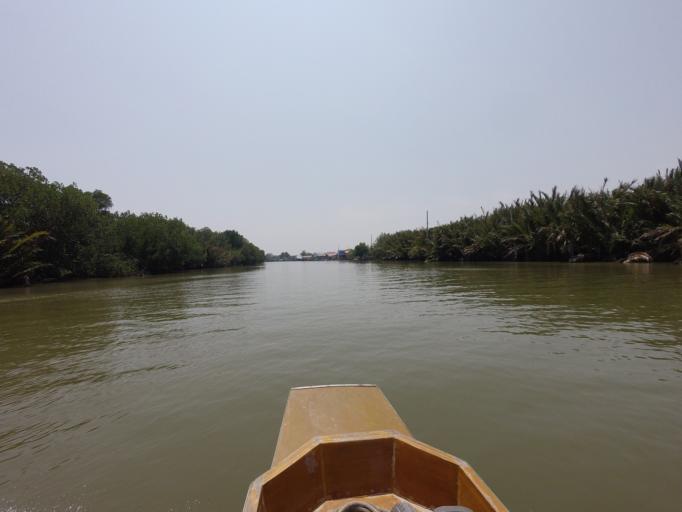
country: TH
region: Bangkok
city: Thung Khru
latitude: 13.5416
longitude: 100.4511
